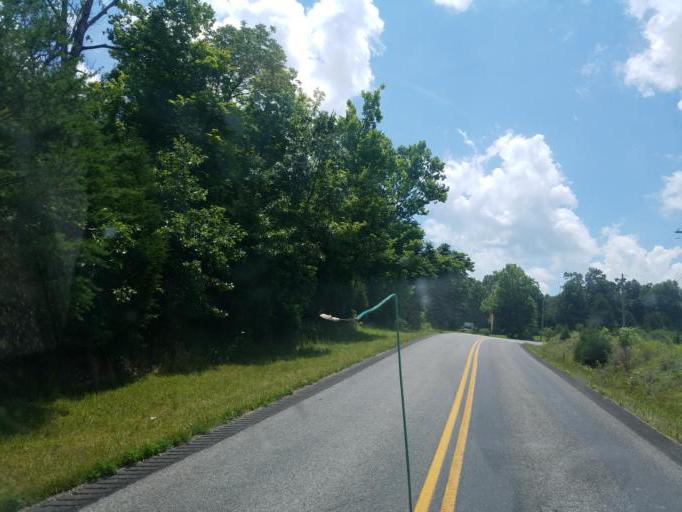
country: US
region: Kentucky
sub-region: Grayson County
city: Leitchfield
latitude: 37.5001
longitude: -86.4758
